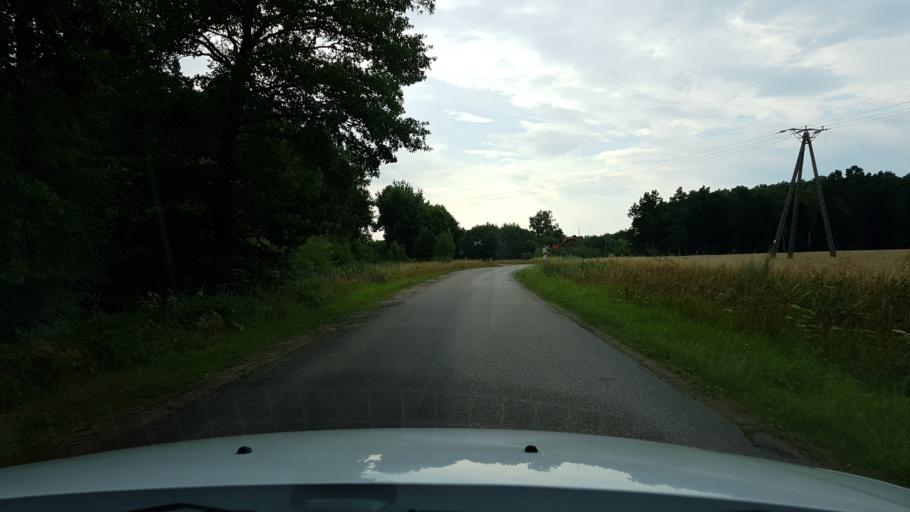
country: PL
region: West Pomeranian Voivodeship
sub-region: Powiat drawski
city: Wierzchowo
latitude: 53.4721
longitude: 16.0716
